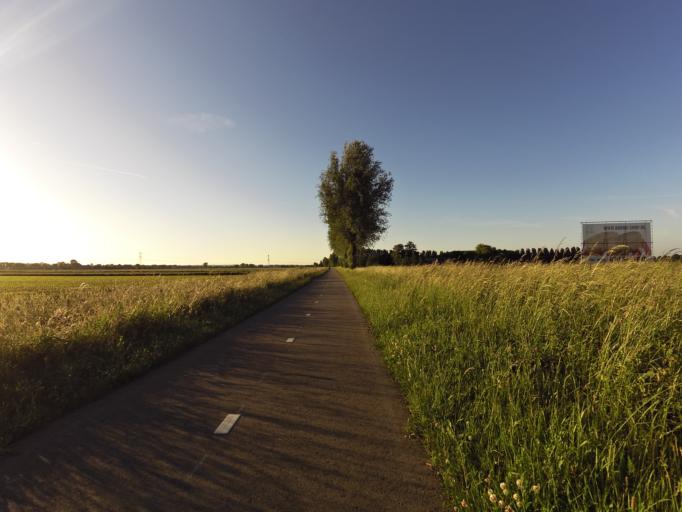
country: NL
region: Gelderland
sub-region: Gemeente Zevenaar
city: Zevenaar
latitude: 51.9458
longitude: 6.0840
